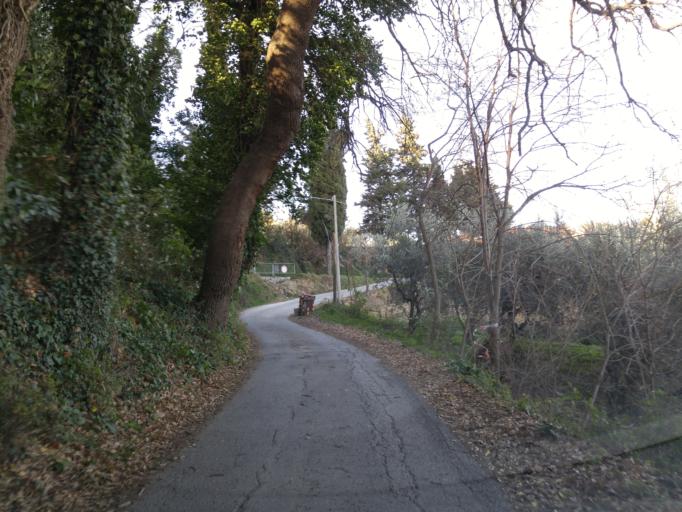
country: IT
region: The Marches
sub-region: Provincia di Pesaro e Urbino
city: Cartoceto
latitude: 43.7631
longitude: 12.8831
